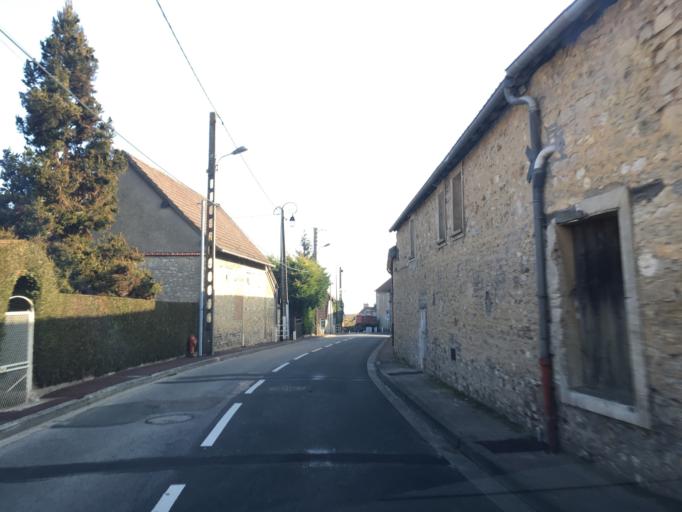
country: FR
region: Haute-Normandie
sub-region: Departement de l'Eure
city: Saint-Marcel
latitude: 49.0945
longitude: 1.4384
